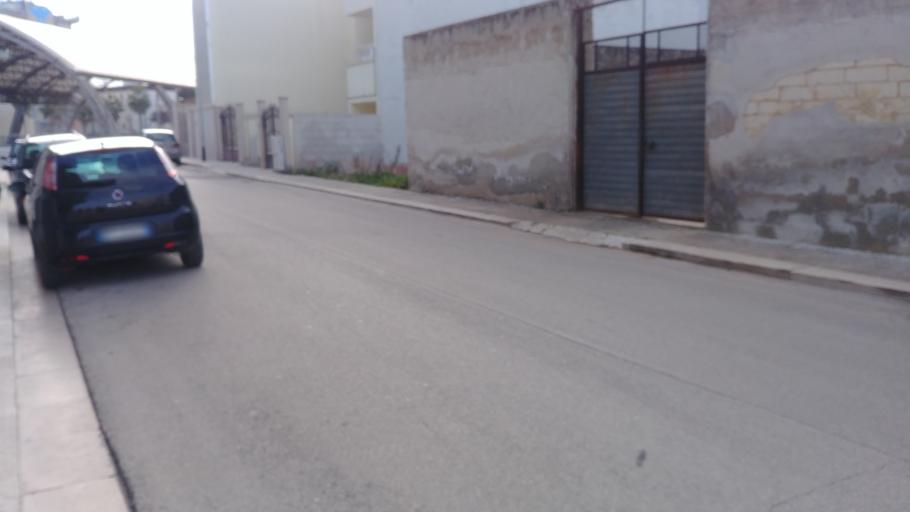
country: IT
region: Apulia
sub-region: Provincia di Barletta - Andria - Trani
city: Andria
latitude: 41.2390
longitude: 16.2955
